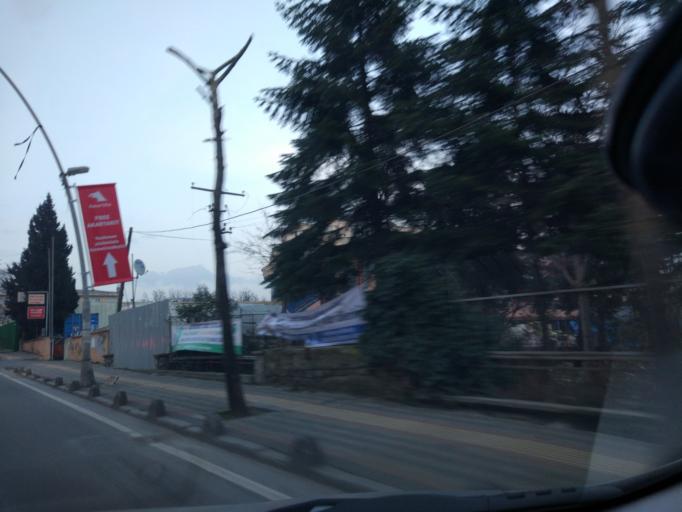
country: TR
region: Istanbul
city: Bahcelievler
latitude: 41.0087
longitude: 28.8224
